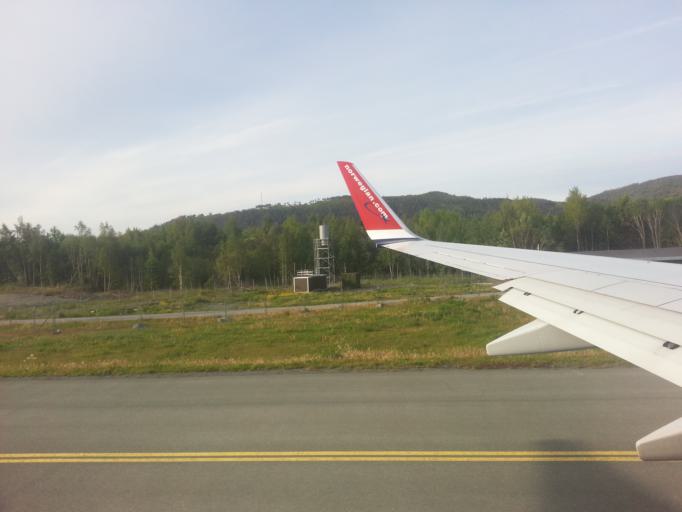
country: NO
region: Nord-Trondelag
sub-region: Stjordal
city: Stjordal
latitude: 63.4560
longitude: 10.9001
